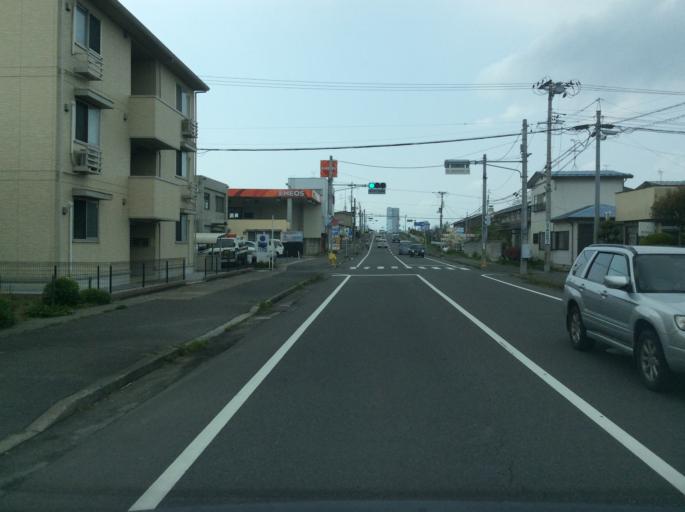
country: JP
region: Fukushima
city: Koriyama
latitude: 37.3842
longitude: 140.4039
